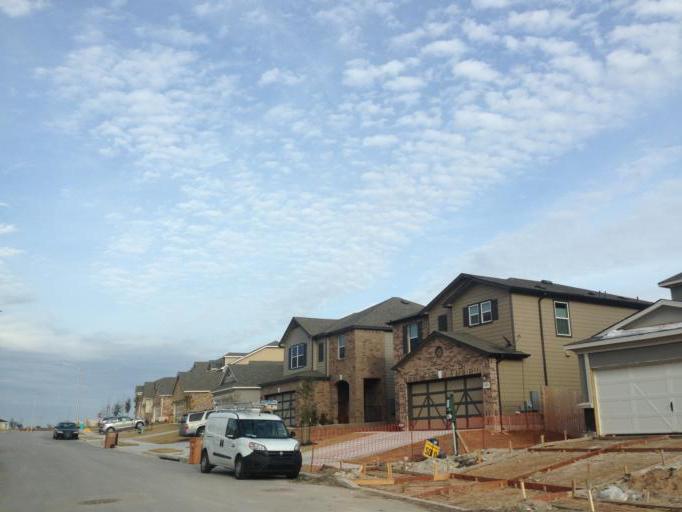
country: US
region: Texas
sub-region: Travis County
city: Wells Branch
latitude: 30.4317
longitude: -97.6569
